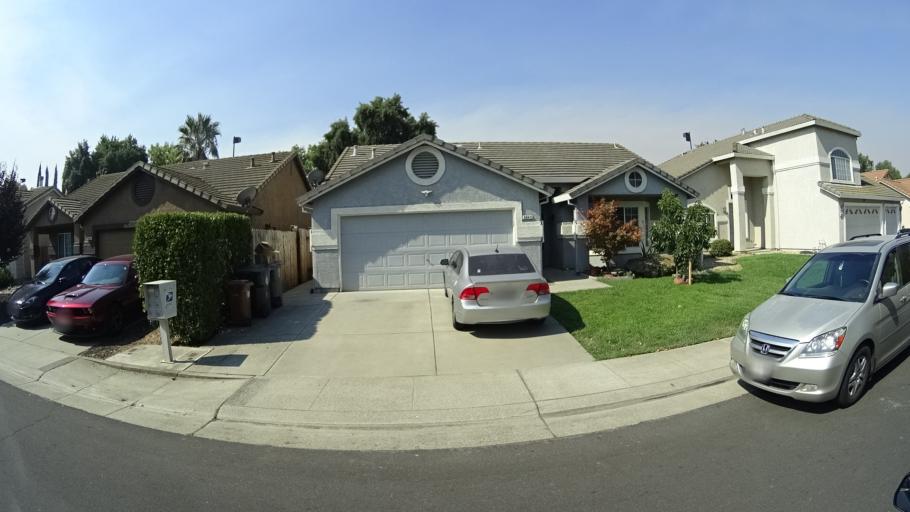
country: US
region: California
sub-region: Sacramento County
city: Laguna
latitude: 38.4265
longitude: -121.4130
